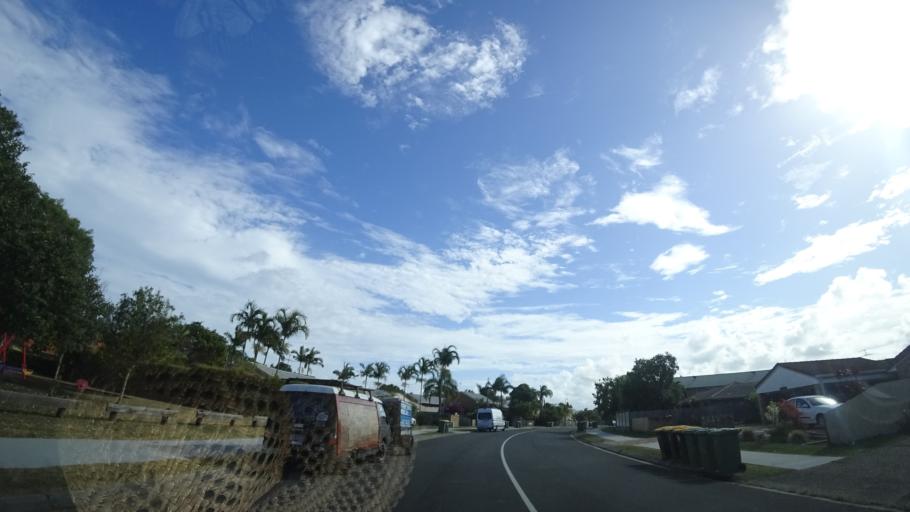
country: AU
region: Queensland
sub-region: Sunshine Coast
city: Coolum Beach
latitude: -26.5633
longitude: 153.0917
